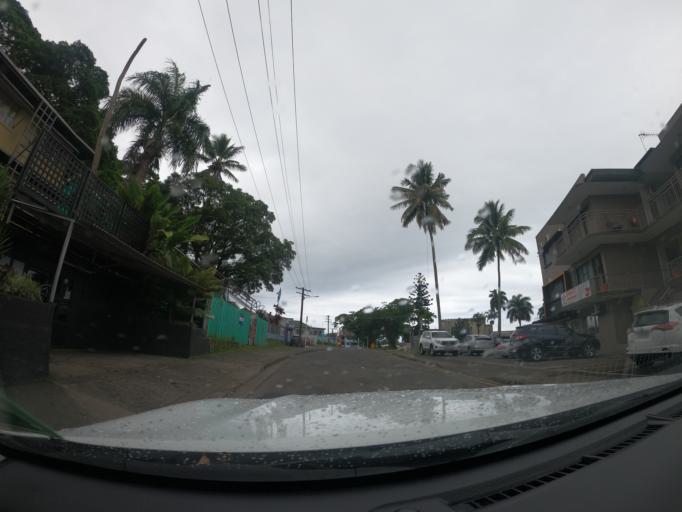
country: FJ
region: Central
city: Suva
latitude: -18.1413
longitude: 178.4247
